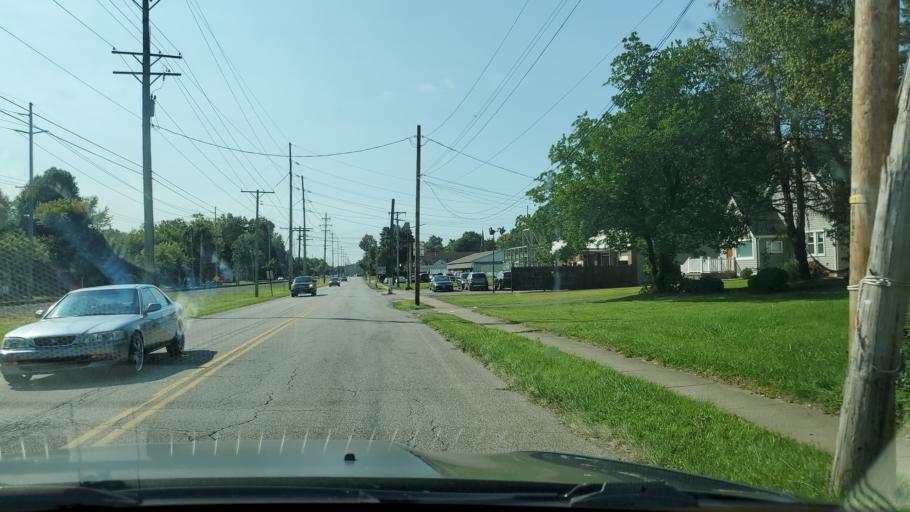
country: US
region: Ohio
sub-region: Mahoning County
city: Boardman
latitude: 41.0514
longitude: -80.6579
